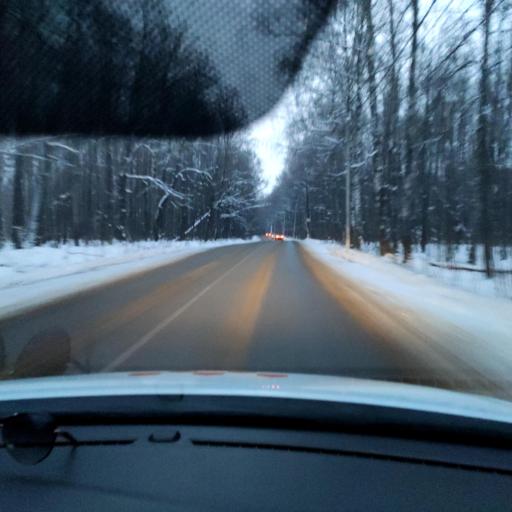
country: RU
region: Tatarstan
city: Vysokaya Gora
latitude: 55.9327
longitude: 49.1858
